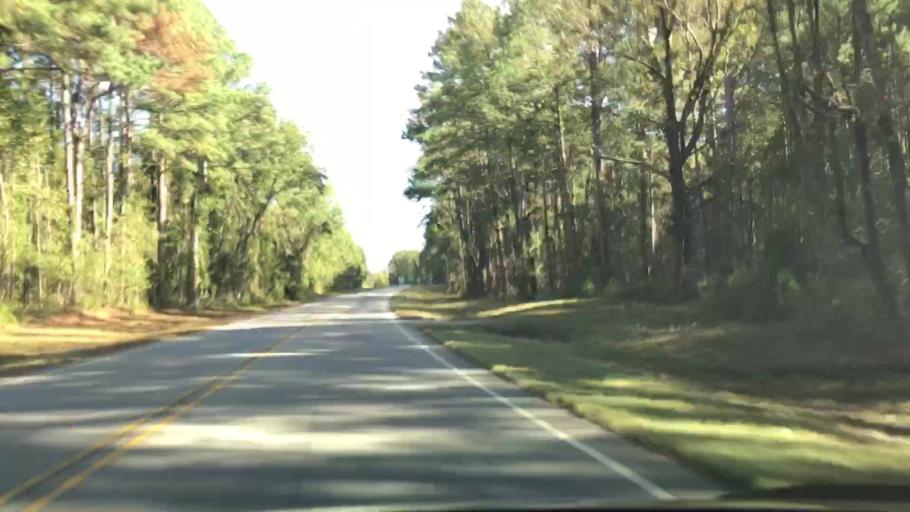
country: US
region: Georgia
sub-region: Warren County
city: Firing Range
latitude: 33.4666
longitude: -82.7136
